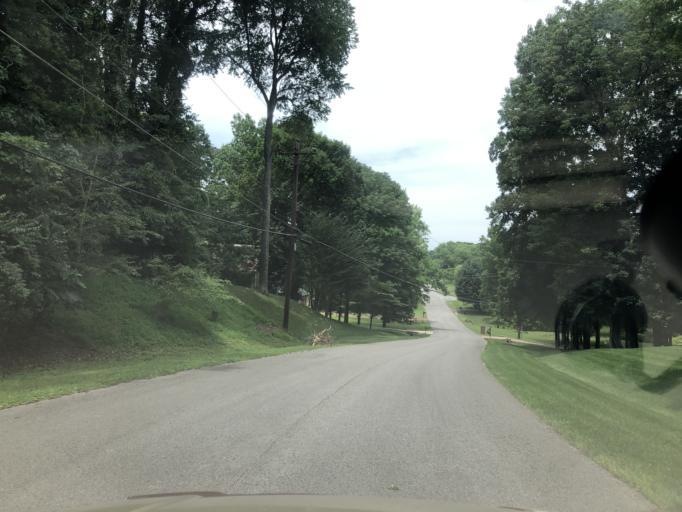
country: US
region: Tennessee
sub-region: Davidson County
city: Lakewood
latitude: 36.2573
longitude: -86.5901
